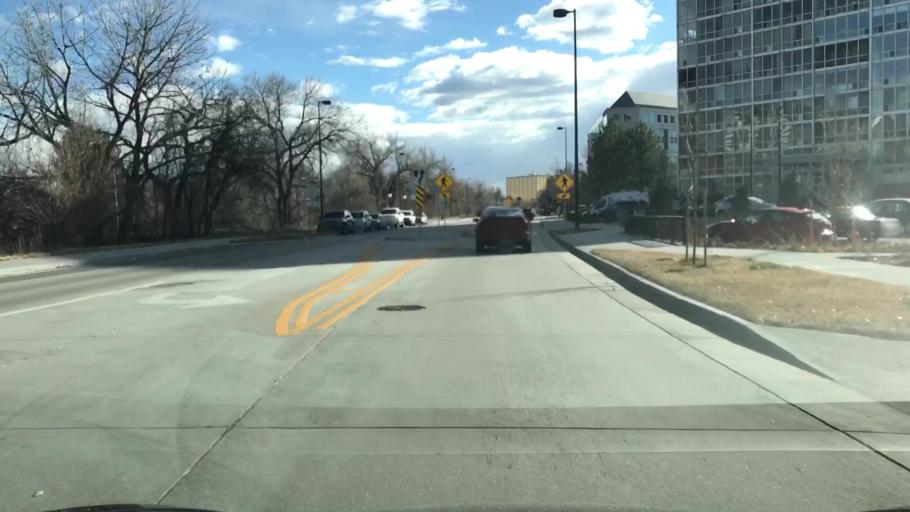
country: US
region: Colorado
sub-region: Arapahoe County
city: Glendale
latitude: 39.7135
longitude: -104.9510
